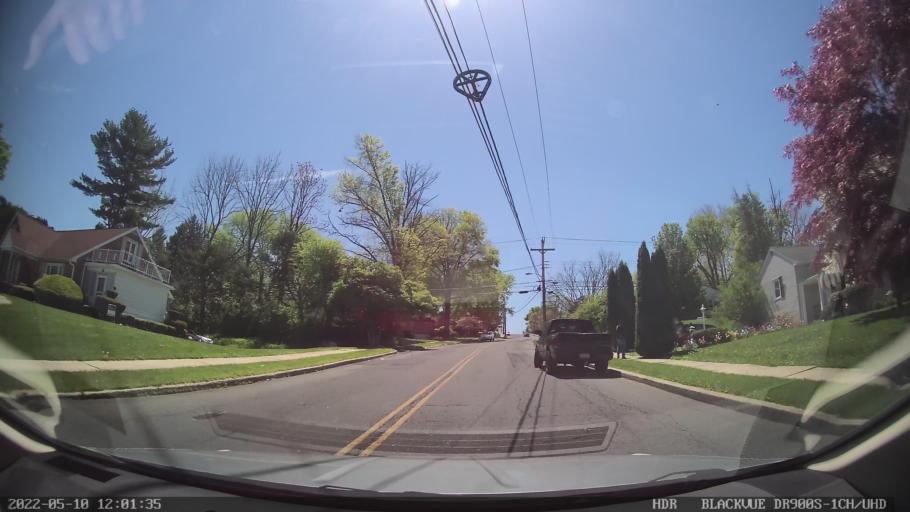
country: US
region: Pennsylvania
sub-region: Berks County
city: West Reading
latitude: 40.3255
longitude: -75.9488
